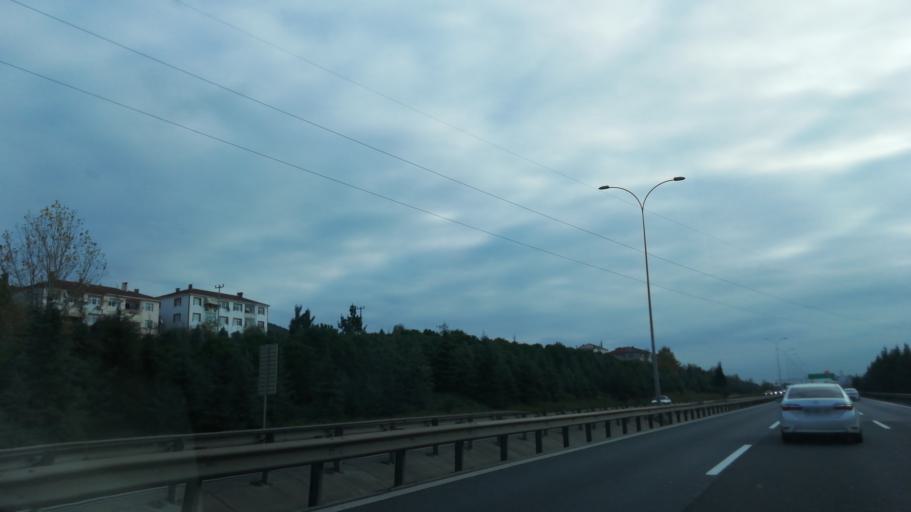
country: TR
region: Kocaeli
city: Korfez
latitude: 40.7748
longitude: 29.7596
